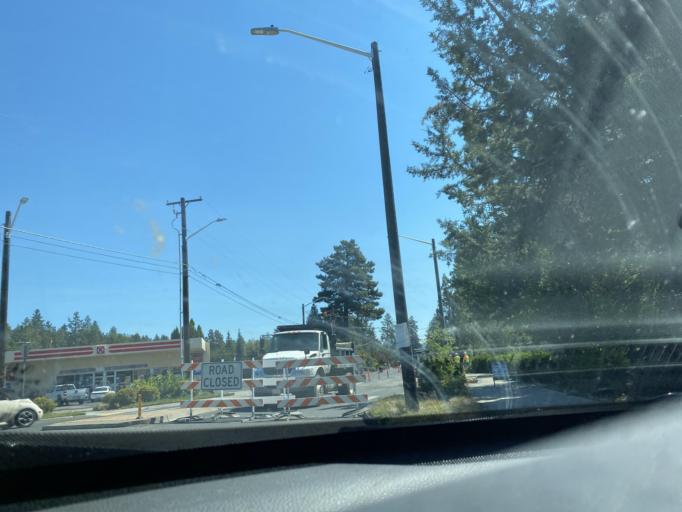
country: US
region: Oregon
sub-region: Deschutes County
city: Bend
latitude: 44.0622
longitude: -121.3380
